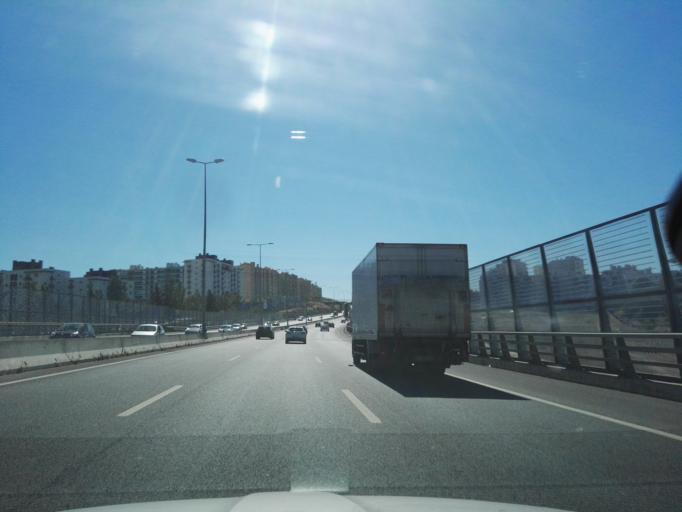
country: PT
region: Lisbon
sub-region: Odivelas
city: Olival do Basto
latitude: 38.7719
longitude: -9.1646
